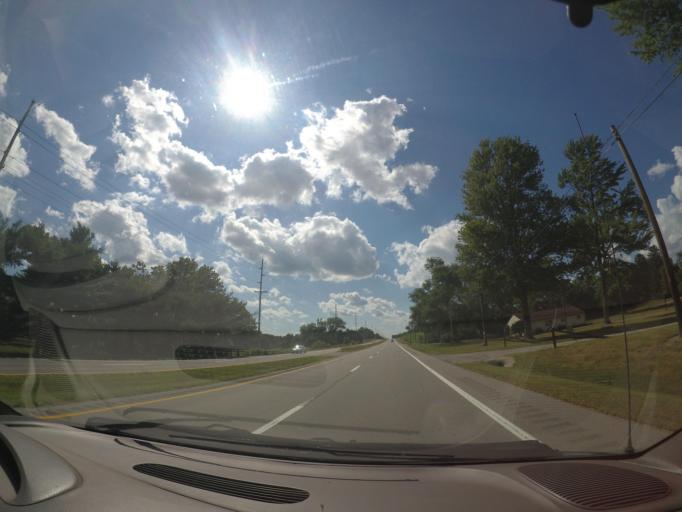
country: US
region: Ohio
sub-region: Sandusky County
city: Mount Carmel
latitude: 41.2922
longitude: -82.9083
